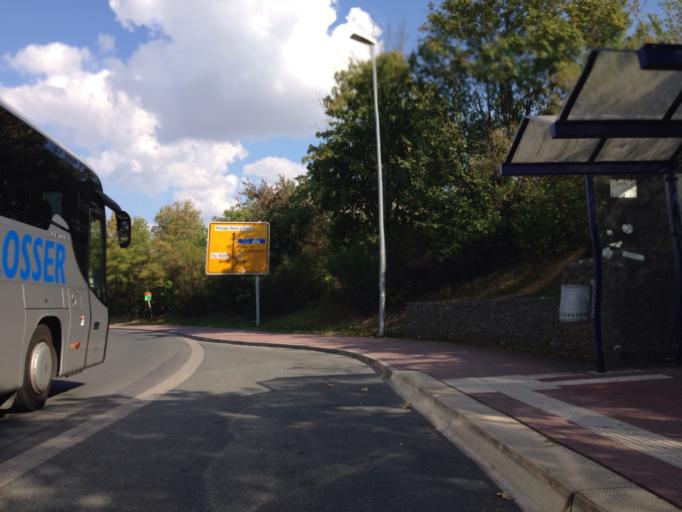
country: DE
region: Hesse
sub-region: Regierungsbezirk Darmstadt
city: Friedrichsdorf
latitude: 50.2571
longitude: 8.6491
